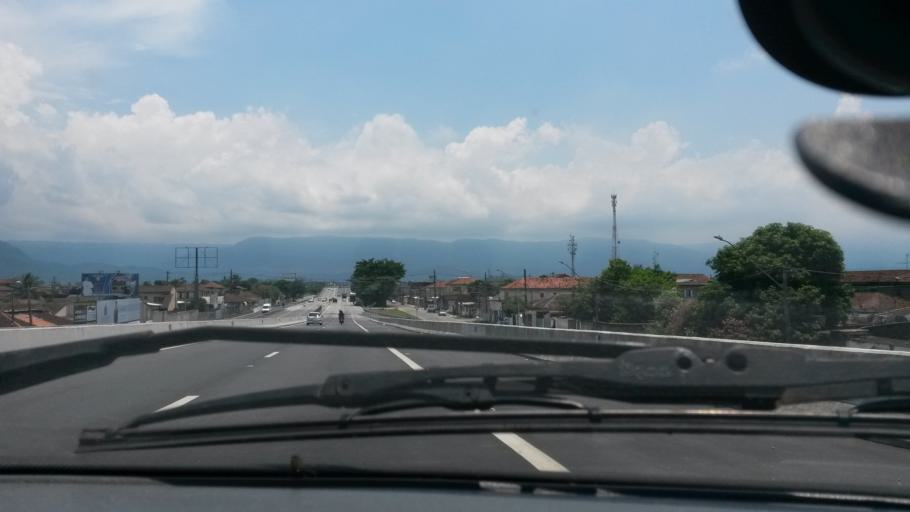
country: BR
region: Sao Paulo
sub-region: Sao Vicente
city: Sao Vicente
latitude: -23.9600
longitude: -46.4053
